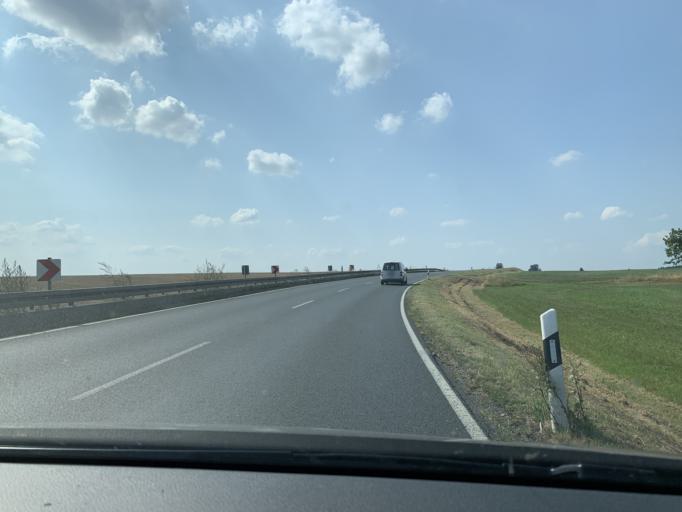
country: DE
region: Saxony
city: Grossschirma
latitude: 51.0039
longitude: 13.2929
